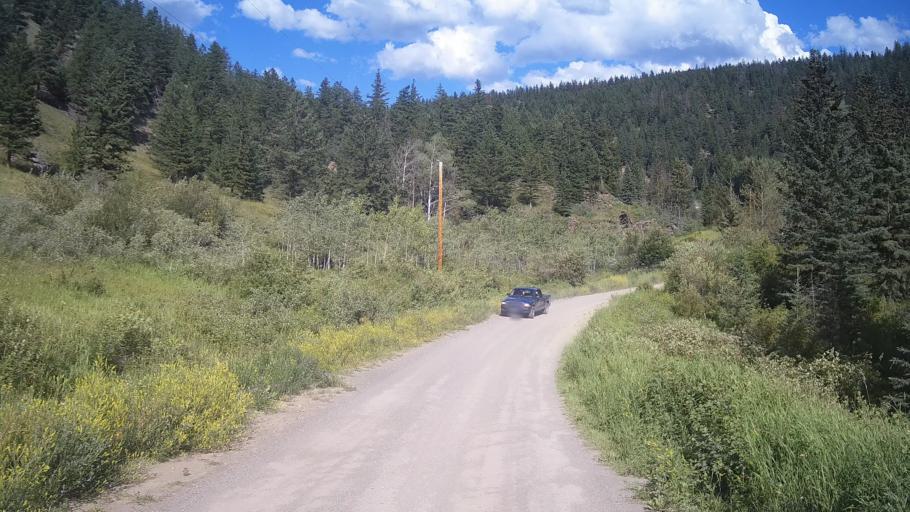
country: CA
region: British Columbia
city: Lillooet
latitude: 51.2586
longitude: -121.9947
